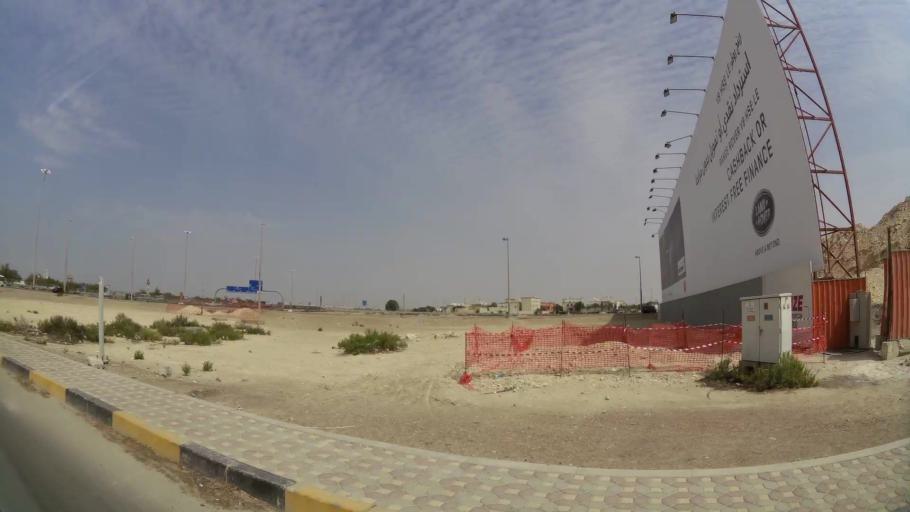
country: AE
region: Abu Dhabi
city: Abu Dhabi
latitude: 24.5346
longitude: 54.6832
